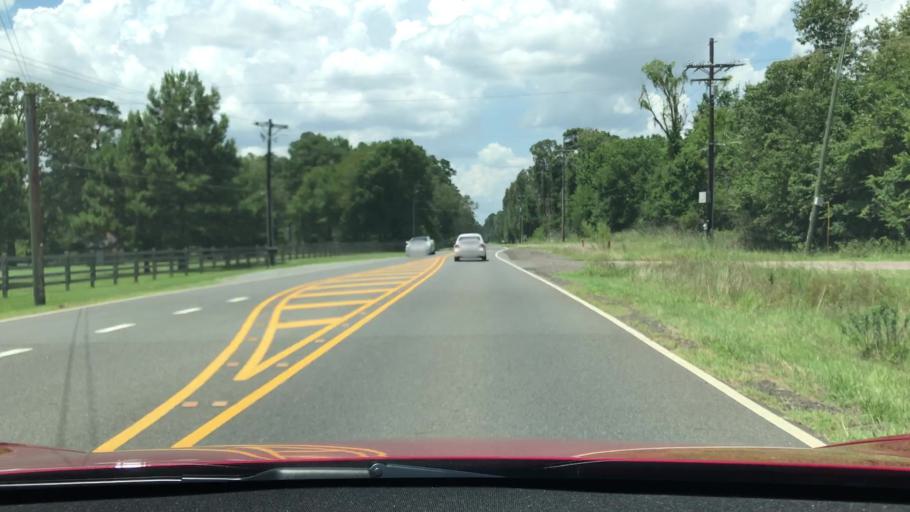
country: US
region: Louisiana
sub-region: De Soto Parish
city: Stonewall
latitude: 32.3646
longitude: -93.6929
